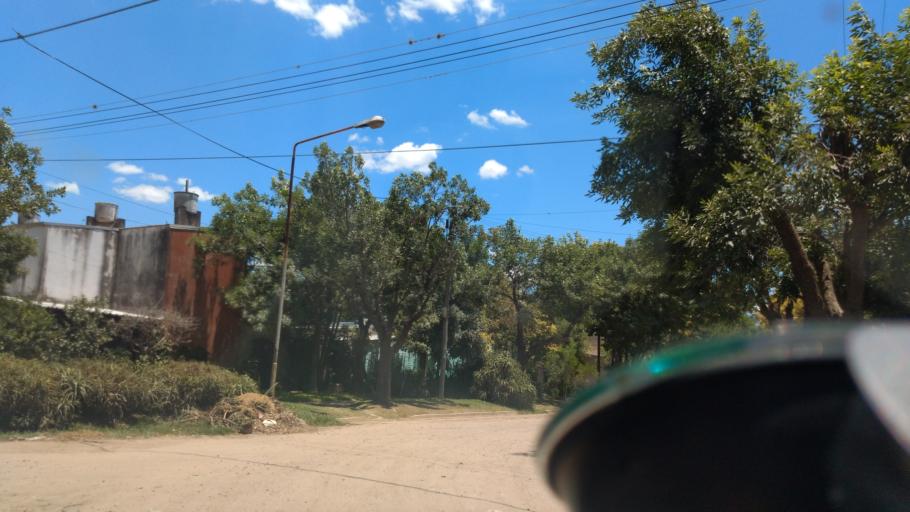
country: AR
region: Santa Fe
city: Laguna Paiva
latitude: -31.3117
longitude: -60.6622
